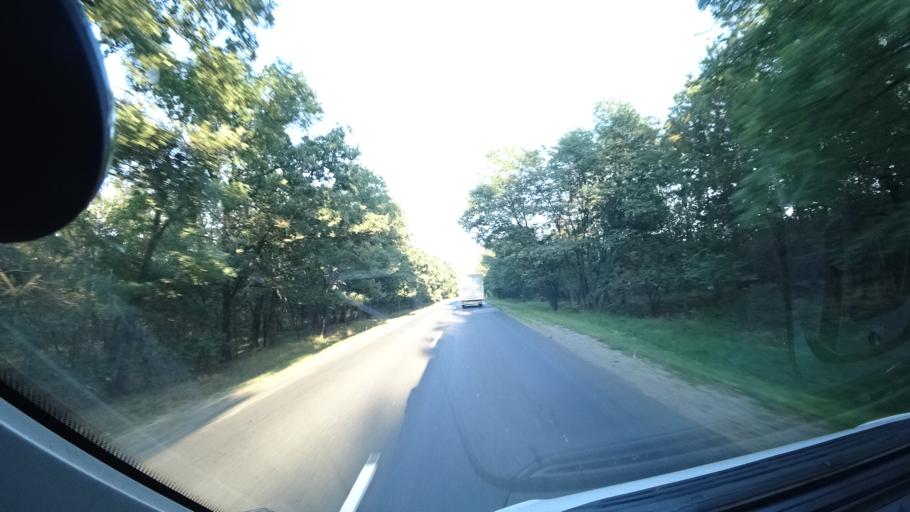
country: PL
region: Opole Voivodeship
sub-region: Powiat kedzierzynsko-kozielski
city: Dziergowice
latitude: 50.2816
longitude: 18.3030
